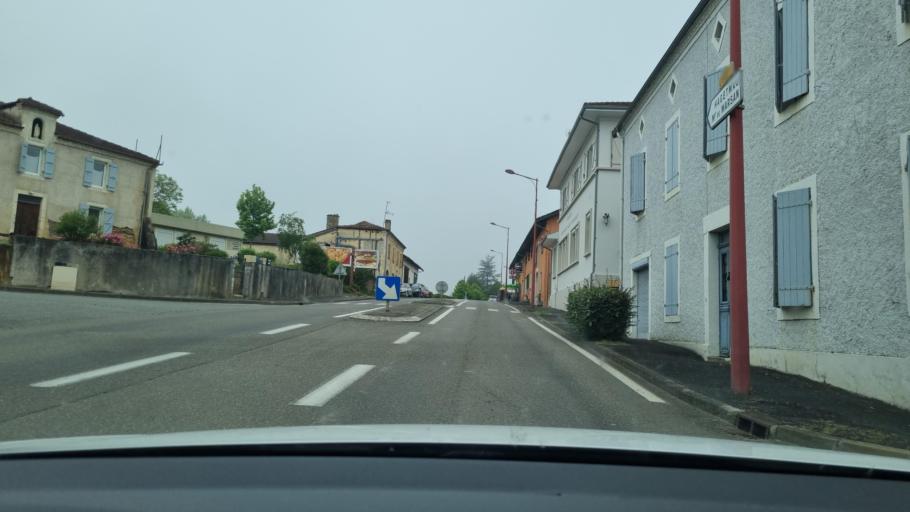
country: FR
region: Aquitaine
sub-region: Departement des Landes
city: Hagetmau
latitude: 43.6137
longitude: -0.6360
